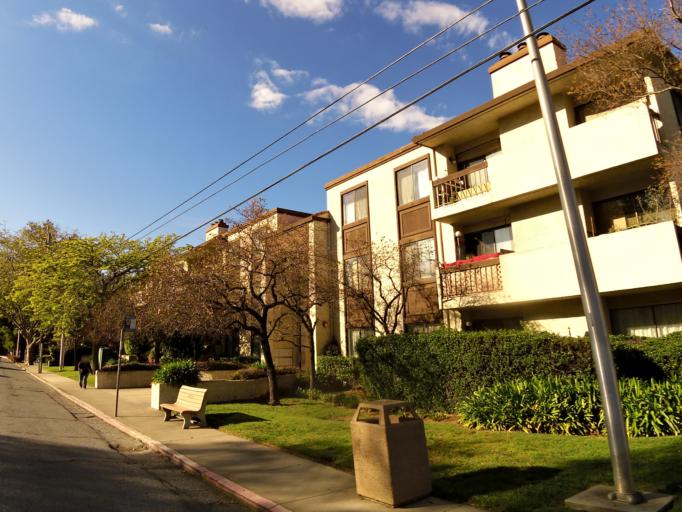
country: US
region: California
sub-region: San Mateo County
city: San Mateo
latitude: 37.5733
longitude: -122.3406
